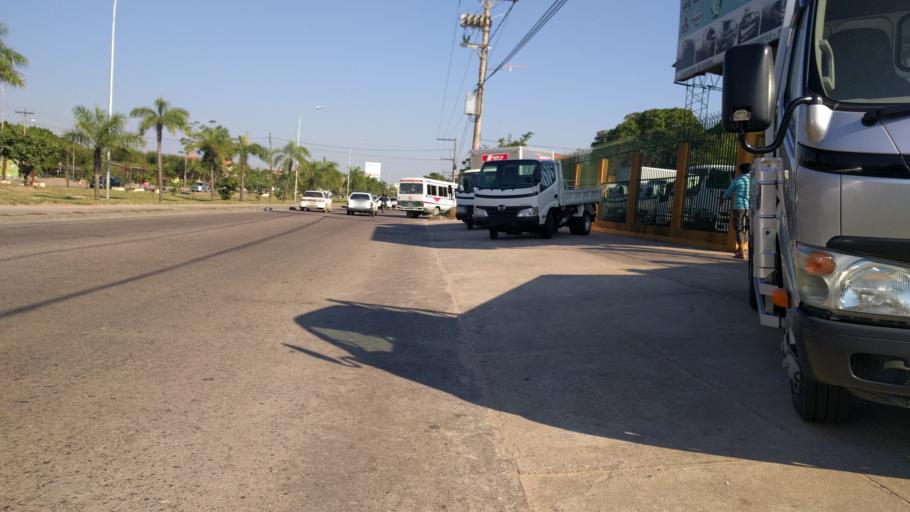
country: BO
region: Santa Cruz
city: Santa Cruz de la Sierra
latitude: -17.8201
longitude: -63.1958
